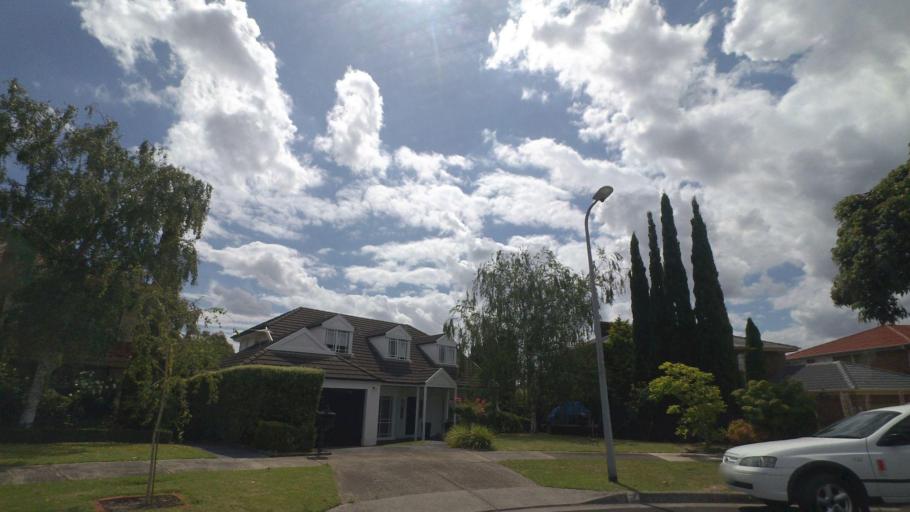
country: AU
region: Victoria
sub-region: Knox
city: Wantirna
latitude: -37.8623
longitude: 145.2167
